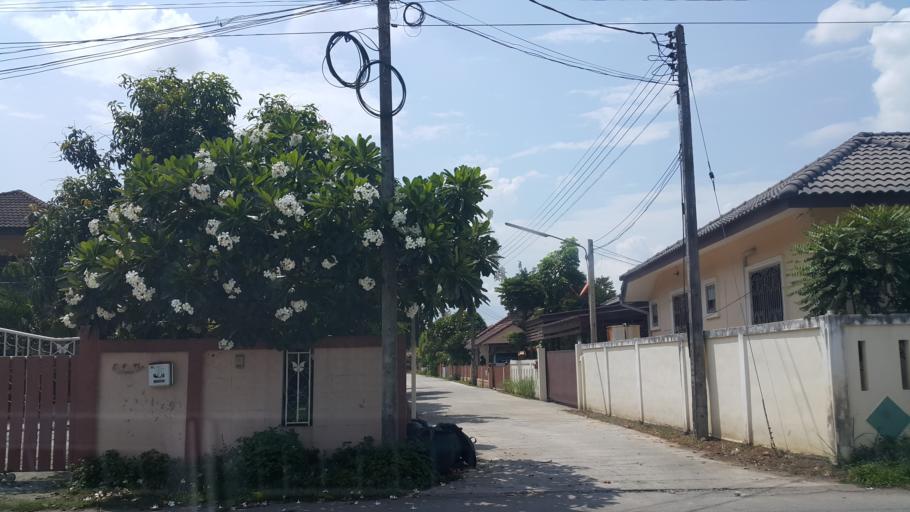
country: TH
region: Chiang Rai
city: Chiang Rai
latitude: 19.9177
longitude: 99.8594
